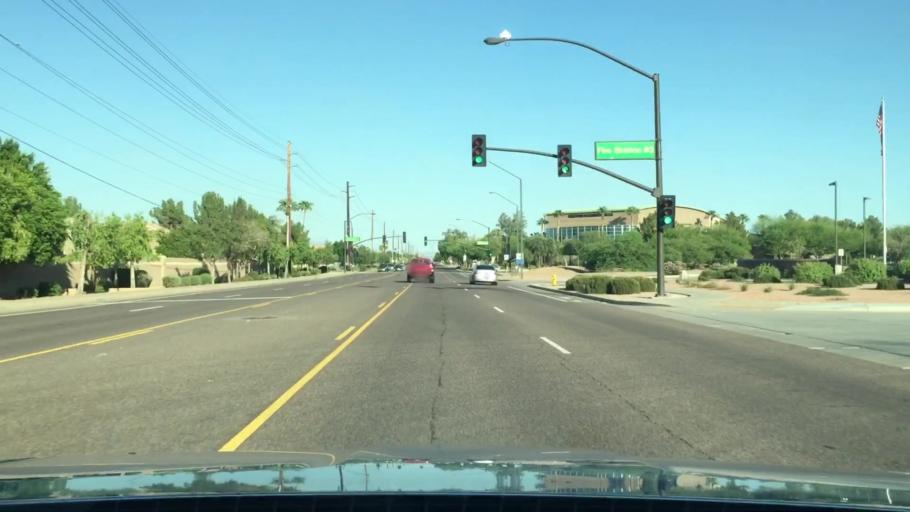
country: US
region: Arizona
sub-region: Maricopa County
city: Gilbert
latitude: 33.3646
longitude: -111.7694
